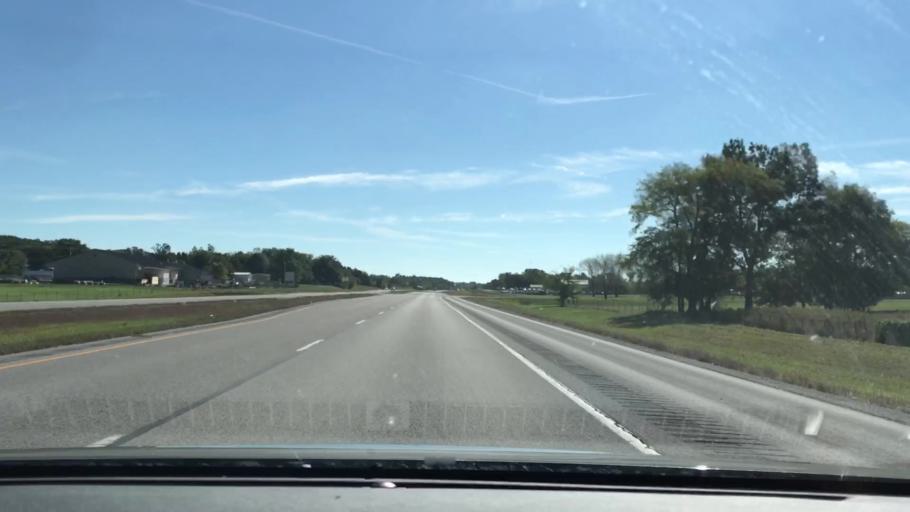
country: US
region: Kentucky
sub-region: Todd County
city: Elkton
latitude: 36.8373
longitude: -87.2400
